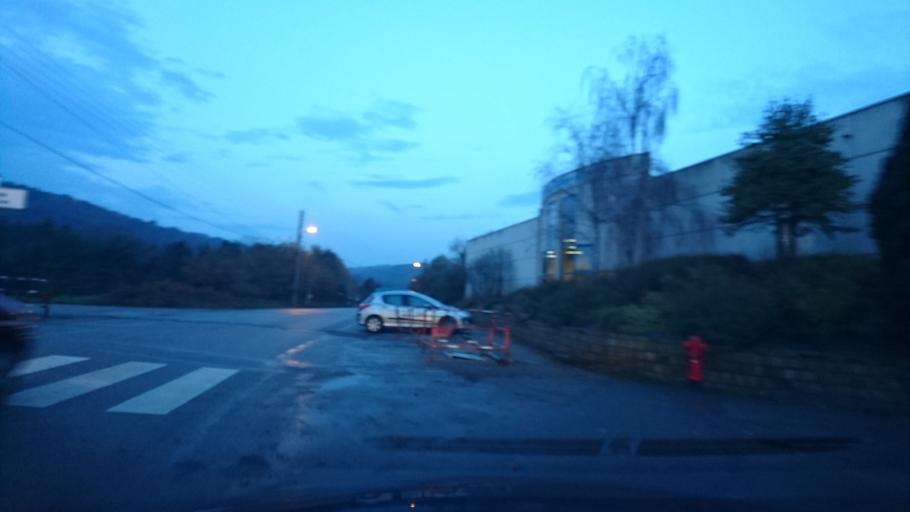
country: FR
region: Brittany
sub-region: Departement du Finistere
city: Chateaulin
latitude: 48.1914
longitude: -4.0882
